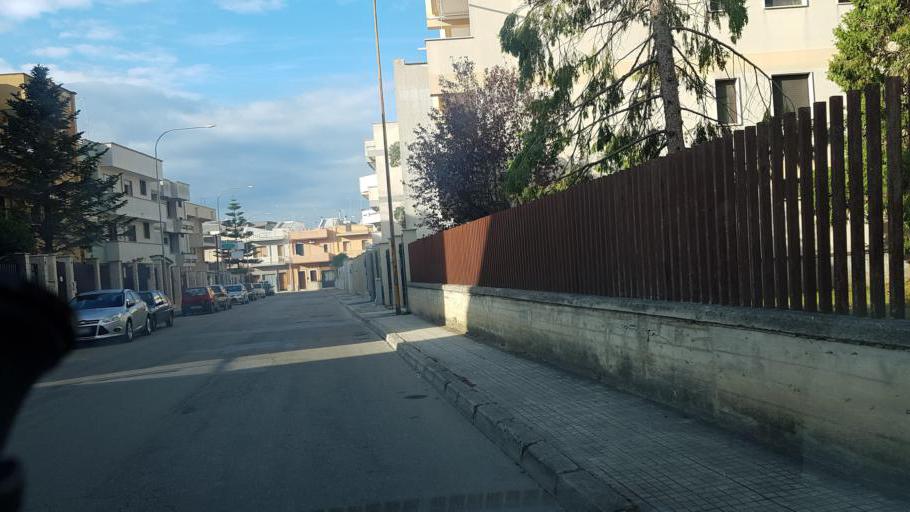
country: IT
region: Apulia
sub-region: Provincia di Brindisi
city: Francavilla Fontana
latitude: 40.5273
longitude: 17.5922
